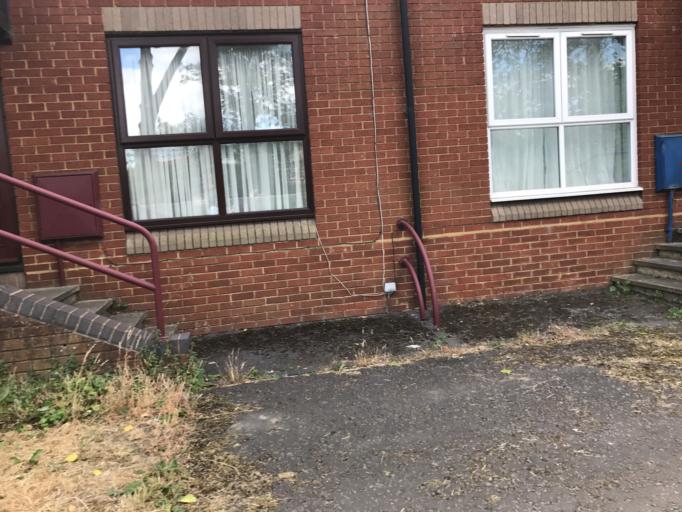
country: GB
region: England
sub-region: Reading
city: Reading
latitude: 51.4557
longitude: -0.9557
